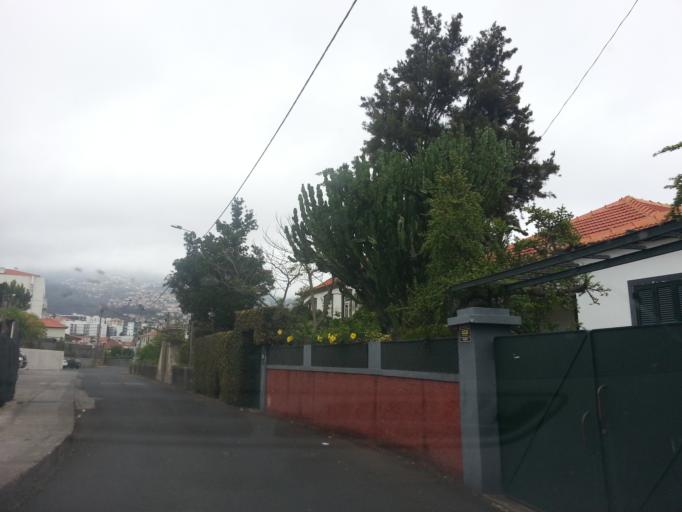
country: PT
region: Madeira
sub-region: Funchal
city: Funchal
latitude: 32.6485
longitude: -16.9291
